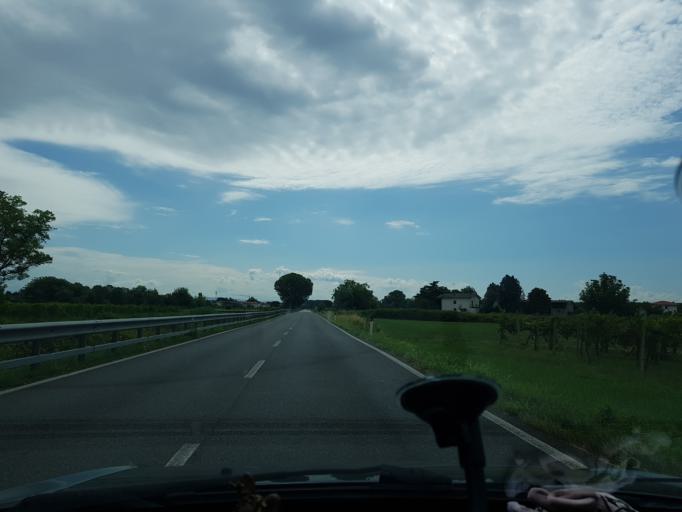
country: IT
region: Friuli Venezia Giulia
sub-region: Provincia di Gorizia
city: San Canzian d'Isonzo
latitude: 45.7962
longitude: 13.4542
